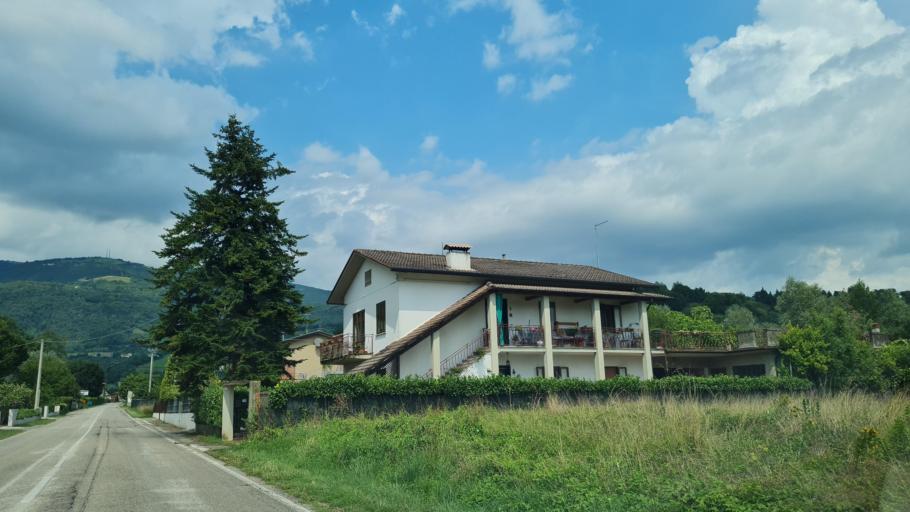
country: IT
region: Veneto
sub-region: Provincia di Vicenza
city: Marostica
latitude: 45.7588
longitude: 11.6607
